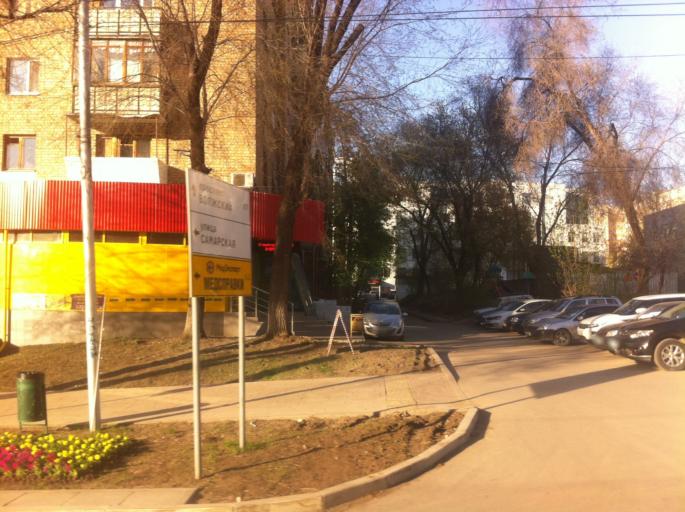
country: RU
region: Samara
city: Samara
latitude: 53.2043
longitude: 50.1250
